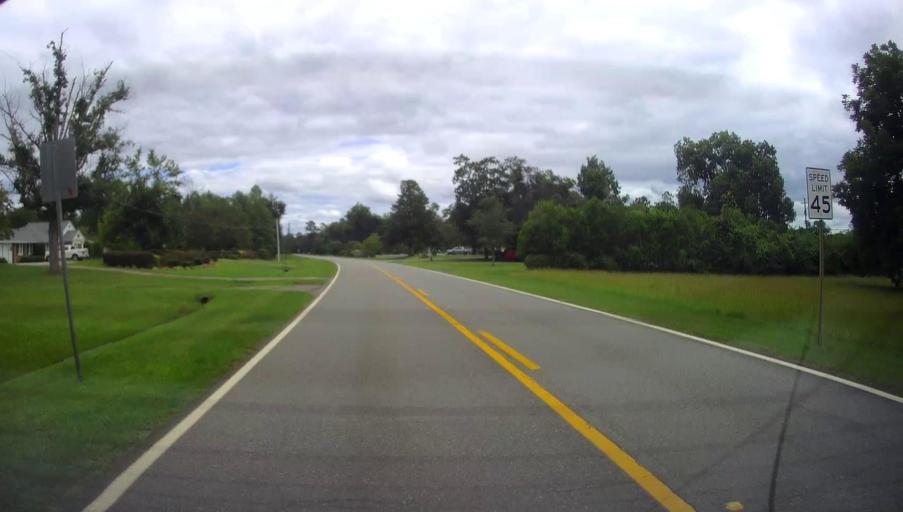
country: US
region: Georgia
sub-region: Twiggs County
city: Jeffersonville
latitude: 32.6809
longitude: -83.3341
